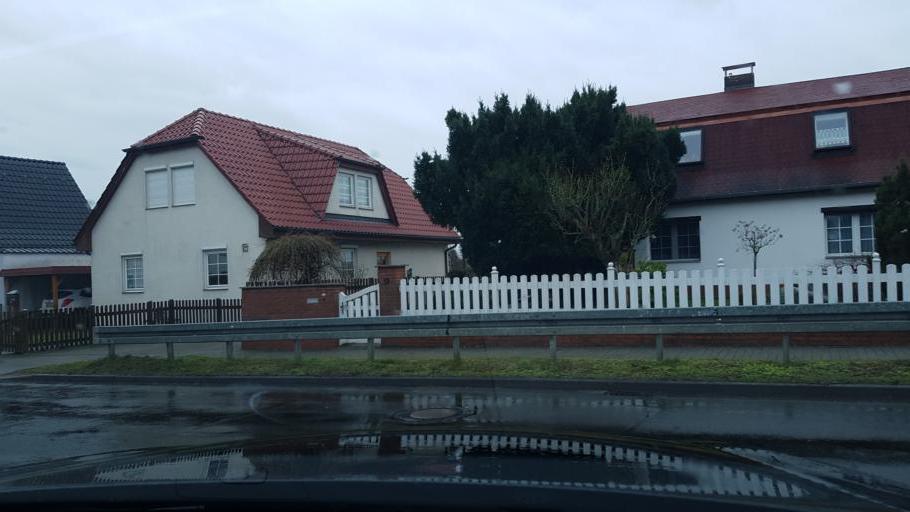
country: DE
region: Berlin
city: Altglienicke
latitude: 52.3965
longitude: 13.5313
